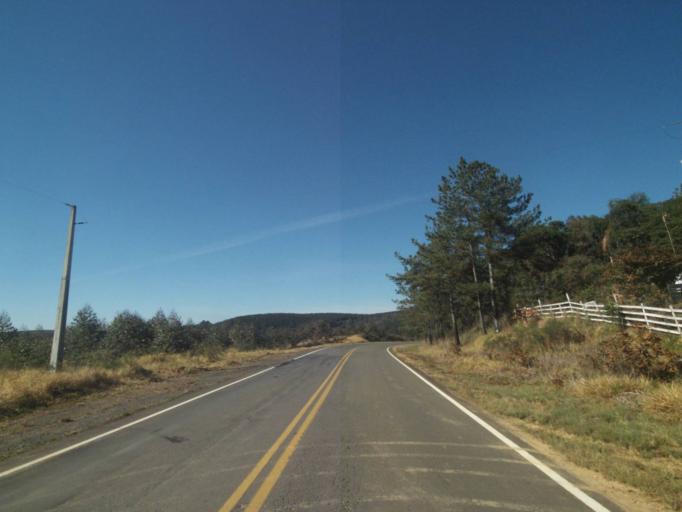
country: BR
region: Parana
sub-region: Telemaco Borba
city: Telemaco Borba
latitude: -24.4207
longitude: -50.5846
